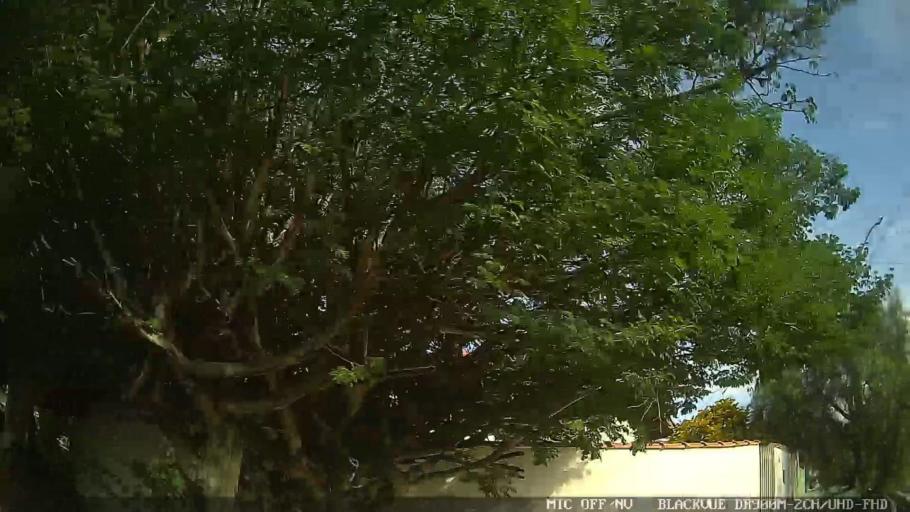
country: BR
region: Sao Paulo
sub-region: Jaguariuna
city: Jaguariuna
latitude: -22.6394
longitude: -47.0572
